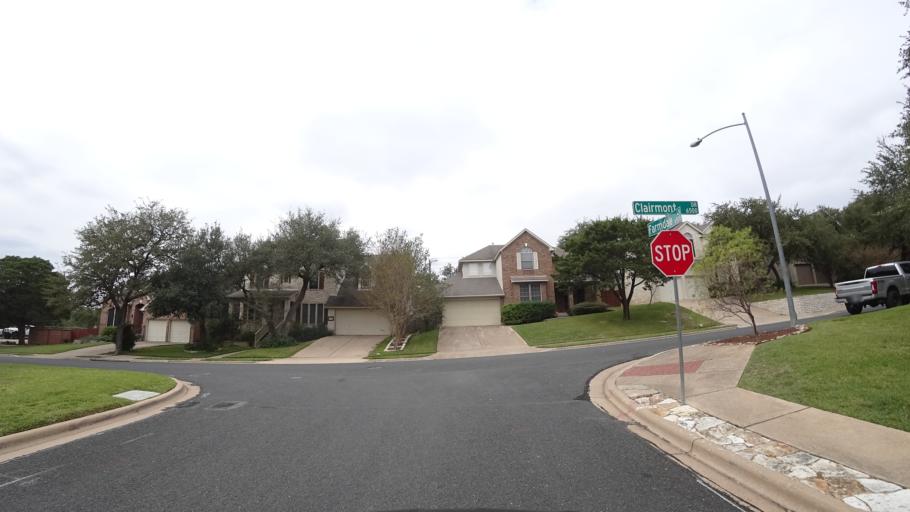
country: US
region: Texas
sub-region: Travis County
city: Shady Hollow
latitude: 30.2139
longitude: -97.8808
